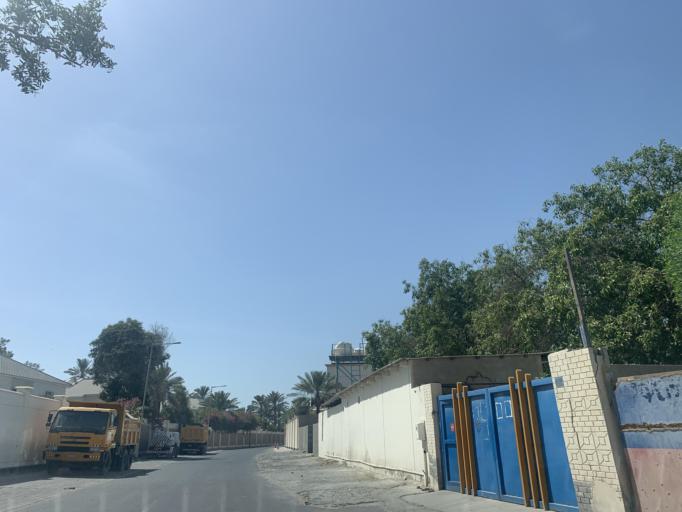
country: BH
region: Manama
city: Jidd Hafs
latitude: 26.2229
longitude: 50.5004
